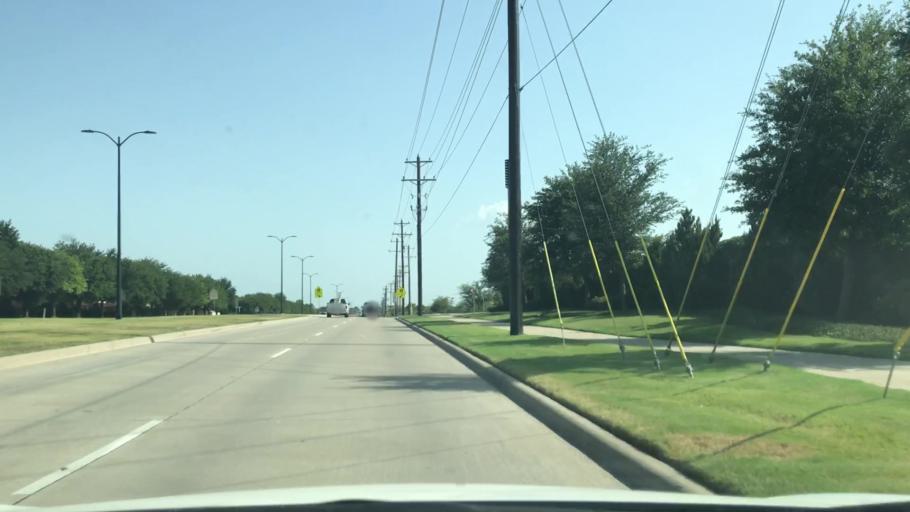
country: US
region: Texas
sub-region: Collin County
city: Frisco
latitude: 33.1298
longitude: -96.7508
